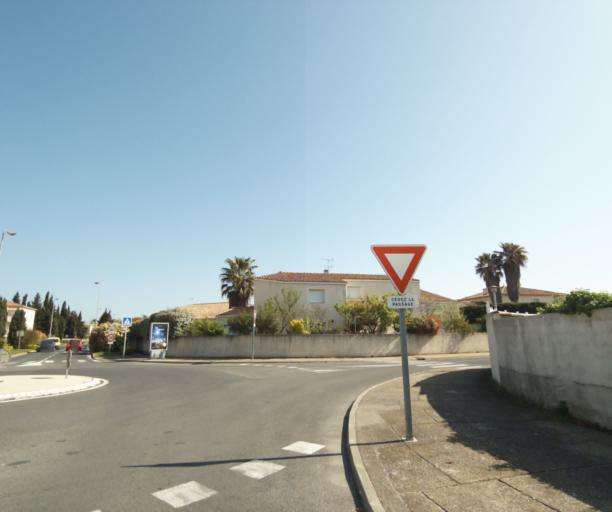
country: FR
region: Languedoc-Roussillon
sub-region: Departement de l'Herault
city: Lattes
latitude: 43.5739
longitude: 3.9060
